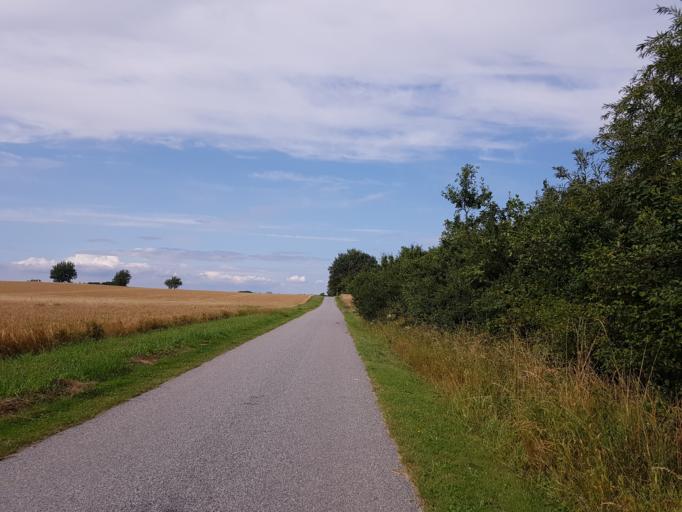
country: DK
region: Zealand
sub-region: Guldborgsund Kommune
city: Nykobing Falster
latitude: 54.5697
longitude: 11.9677
